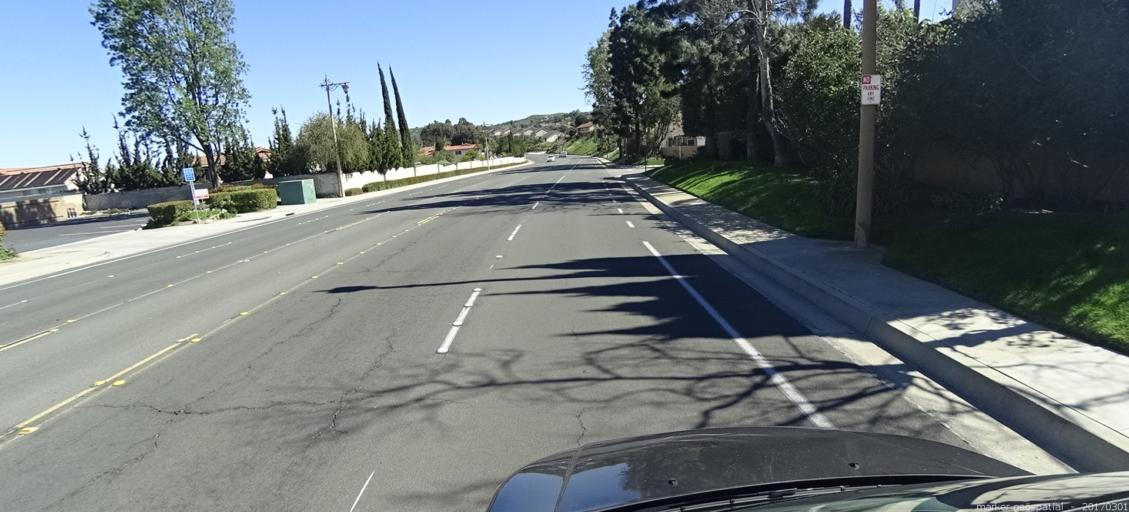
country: US
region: California
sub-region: Orange County
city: Villa Park
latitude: 33.8313
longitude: -117.7595
